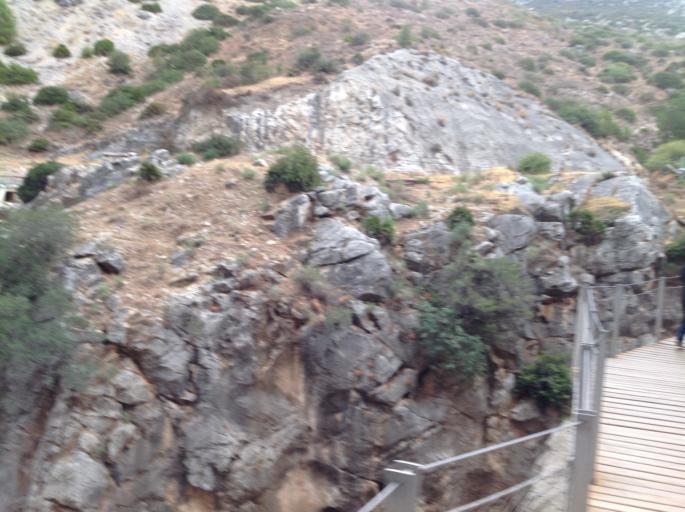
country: ES
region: Andalusia
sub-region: Provincia de Malaga
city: Ardales
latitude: 36.9287
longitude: -4.7830
